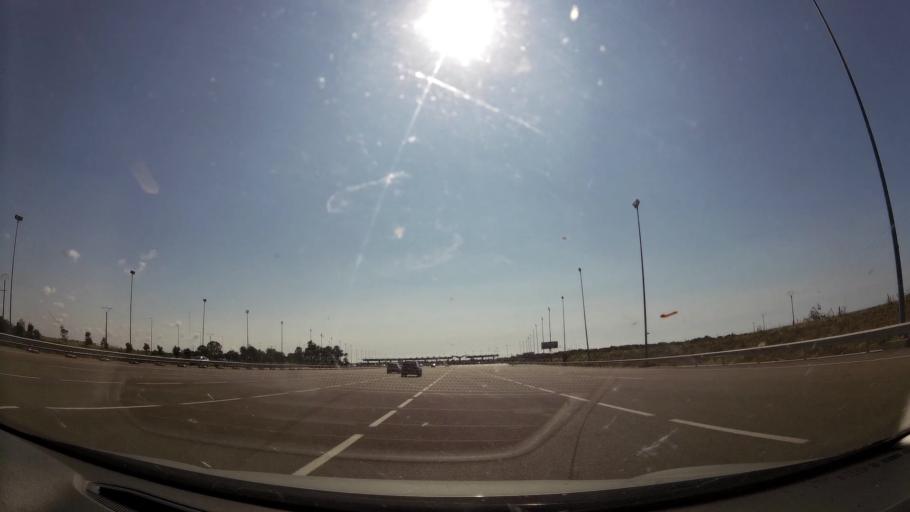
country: MA
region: Chaouia-Ouardigha
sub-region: Benslimane
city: Bouznika
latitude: 33.7986
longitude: -7.1690
